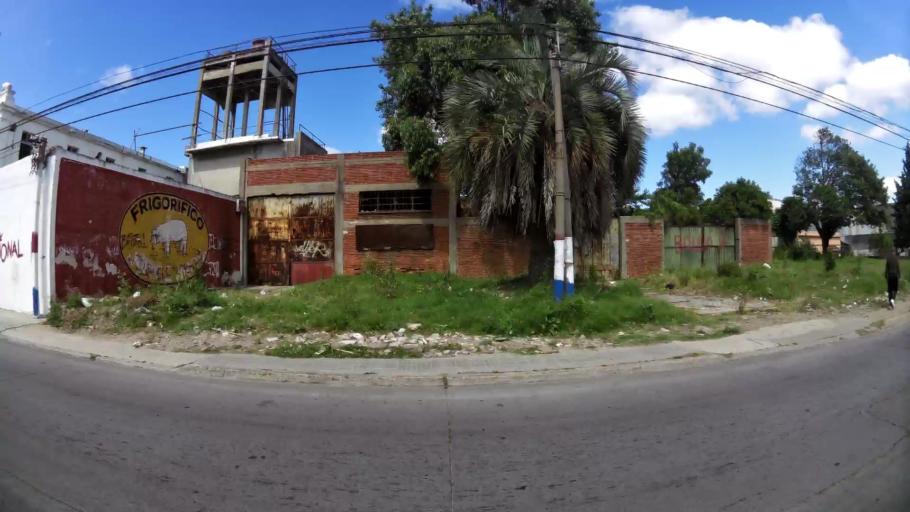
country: UY
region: Montevideo
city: Montevideo
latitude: -34.8627
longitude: -56.1393
